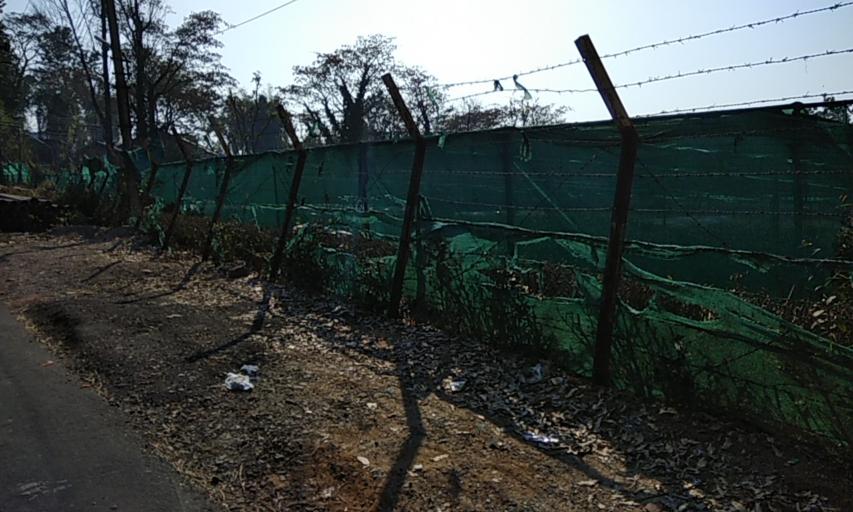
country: IN
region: Himachal Pradesh
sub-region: Kangra
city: Palampur
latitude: 32.1184
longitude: 76.5252
